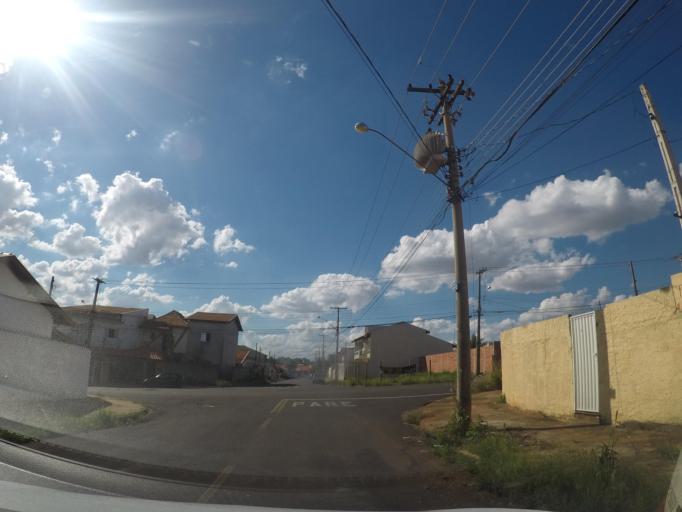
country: BR
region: Sao Paulo
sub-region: Sumare
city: Sumare
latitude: -22.8322
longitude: -47.2799
